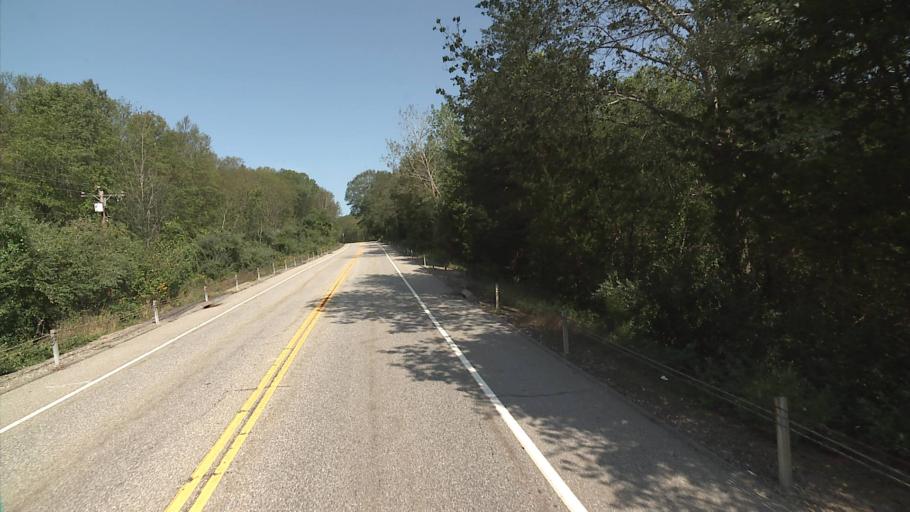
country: US
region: Connecticut
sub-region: Windham County
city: East Brooklyn
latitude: 41.8035
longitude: -71.9506
